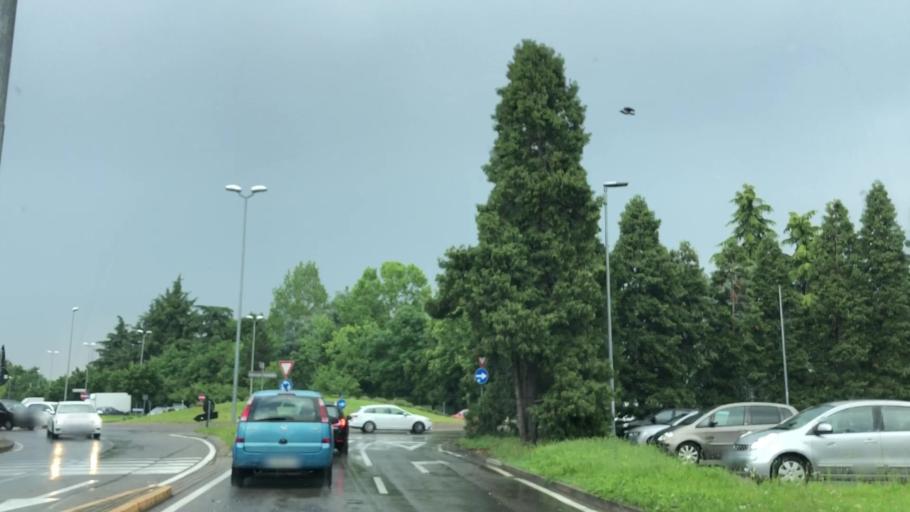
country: IT
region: Lombardy
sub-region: Citta metropolitana di Milano
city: Paderno Dugnano
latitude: 45.5690
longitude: 9.1717
